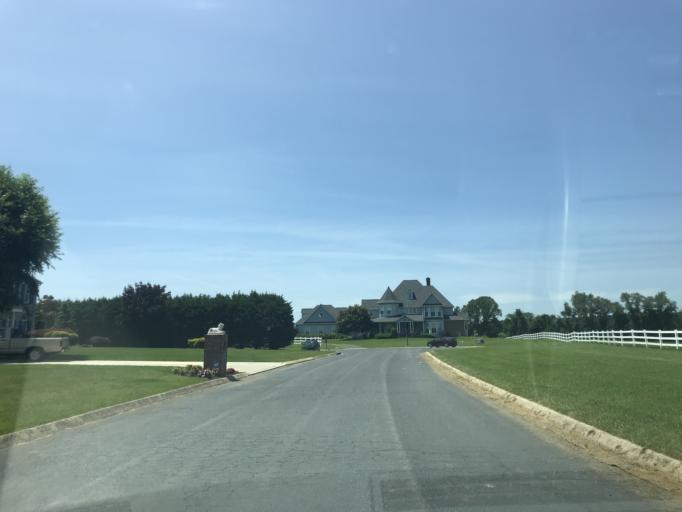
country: US
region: Maryland
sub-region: Harford County
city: Bel Air South
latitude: 39.5515
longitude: -76.2765
